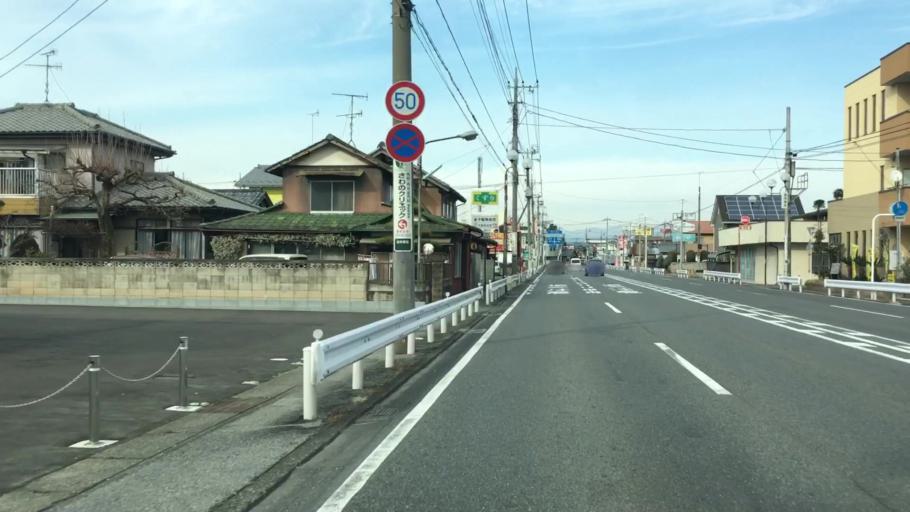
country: JP
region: Saitama
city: Menuma
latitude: 36.2577
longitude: 139.3773
